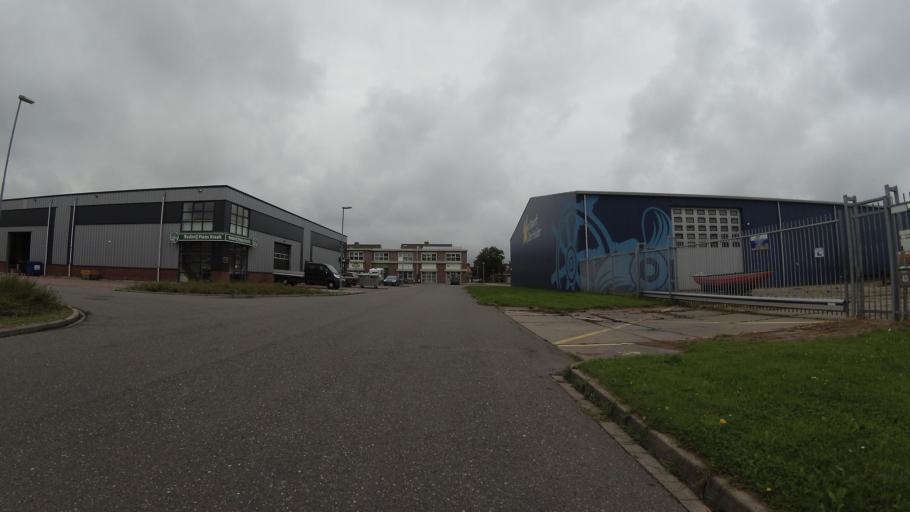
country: NL
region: North Holland
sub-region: Gemeente Den Helder
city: Den Helder
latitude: 52.9492
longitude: 4.7713
